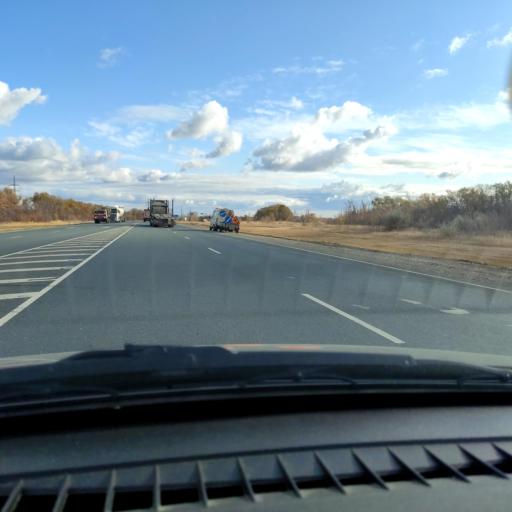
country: RU
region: Samara
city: Varlamovo
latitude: 53.1963
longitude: 48.3025
